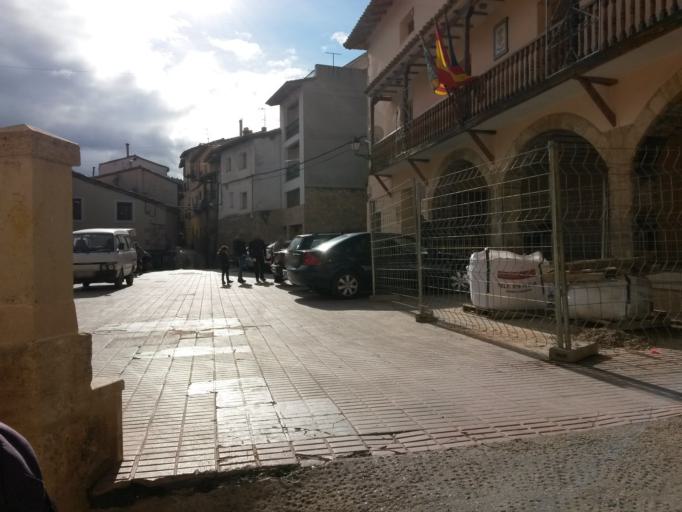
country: ES
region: Valencia
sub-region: Provincia de Valencia
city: Ademuz
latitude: 40.0609
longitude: -1.2860
